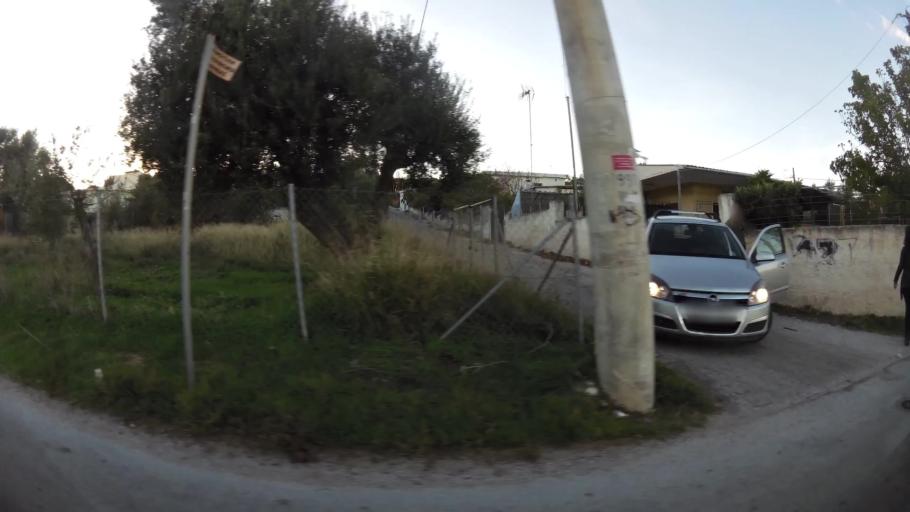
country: GR
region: Attica
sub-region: Nomarchia Anatolikis Attikis
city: Rafina
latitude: 38.0109
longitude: 24.0108
